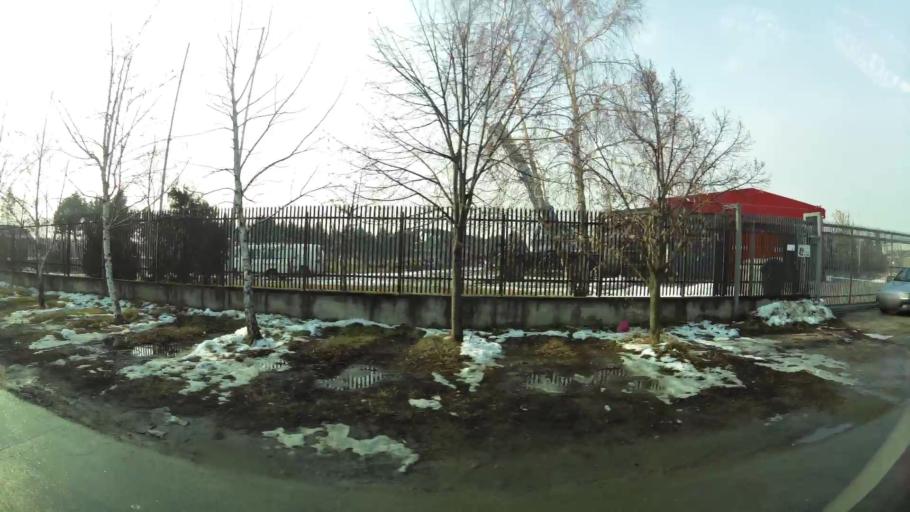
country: MK
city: Kadino
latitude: 41.9753
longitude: 21.5982
